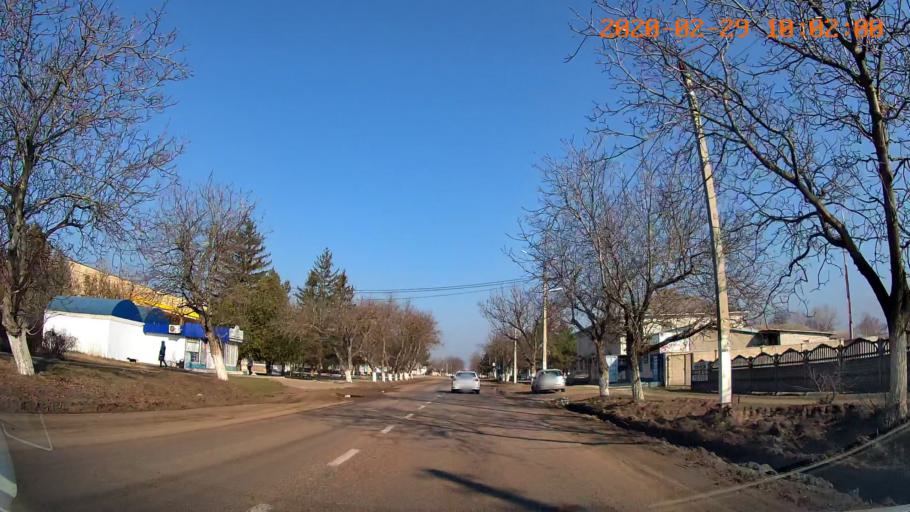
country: MD
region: Telenesti
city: Slobozia
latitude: 46.7794
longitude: 29.6841
